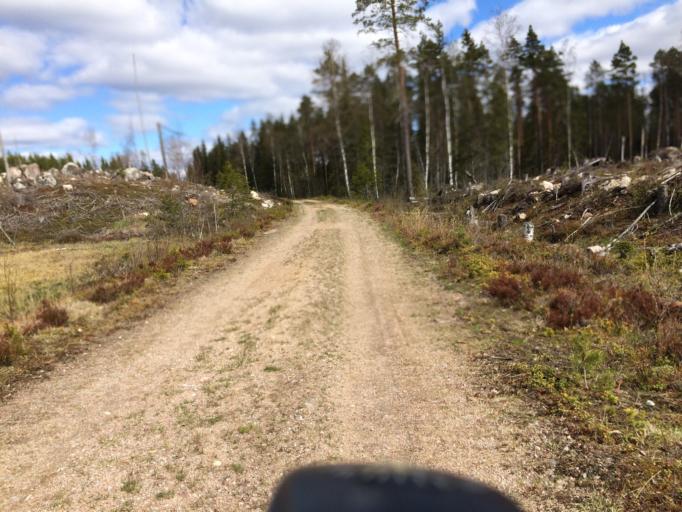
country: SE
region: OErebro
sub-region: Hallefors Kommun
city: Haellefors
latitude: 60.0536
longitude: 14.5236
